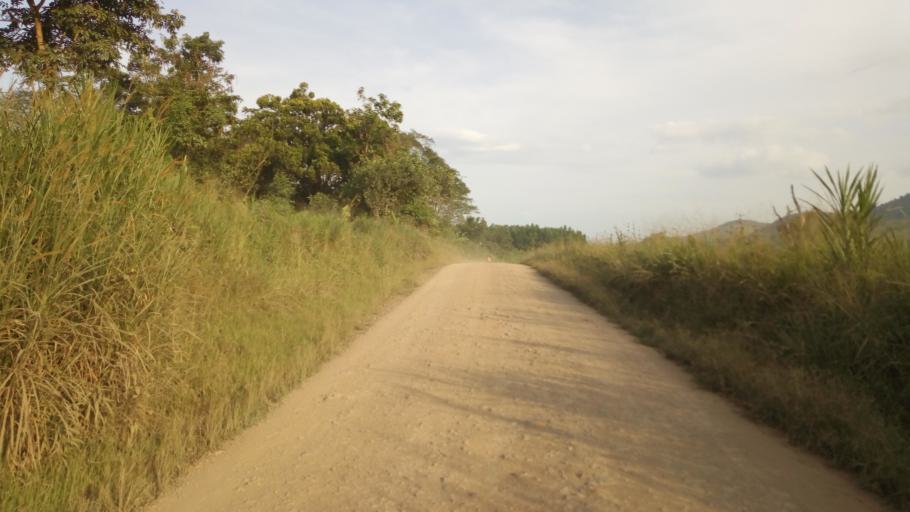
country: UG
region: Central Region
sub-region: Kiboga District
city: Kiboga
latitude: 0.7156
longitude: 31.7477
